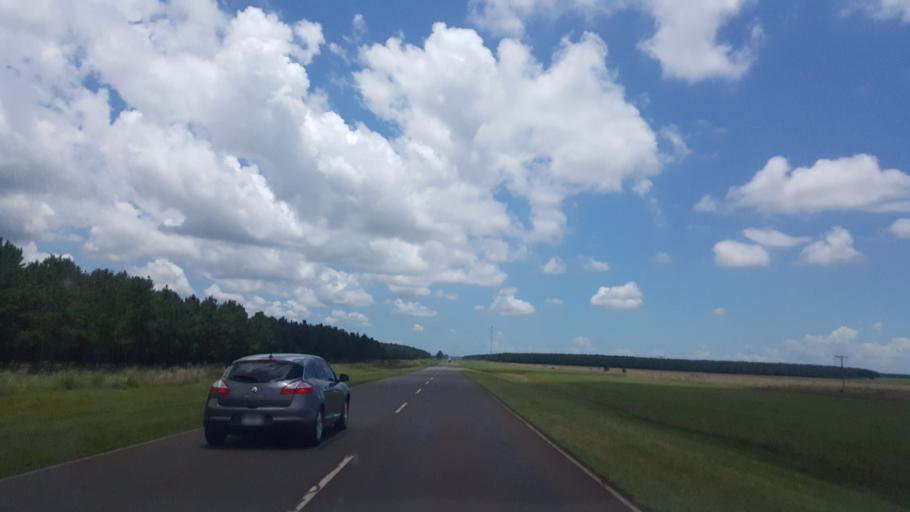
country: PY
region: Itapua
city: San Juan del Parana
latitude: -27.5130
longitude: -56.1412
